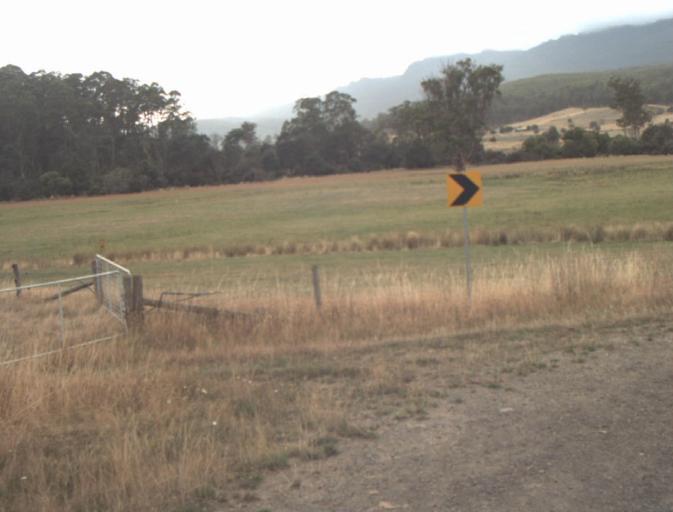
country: AU
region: Tasmania
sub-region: Northern Midlands
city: Evandale
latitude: -41.4639
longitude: 147.5369
